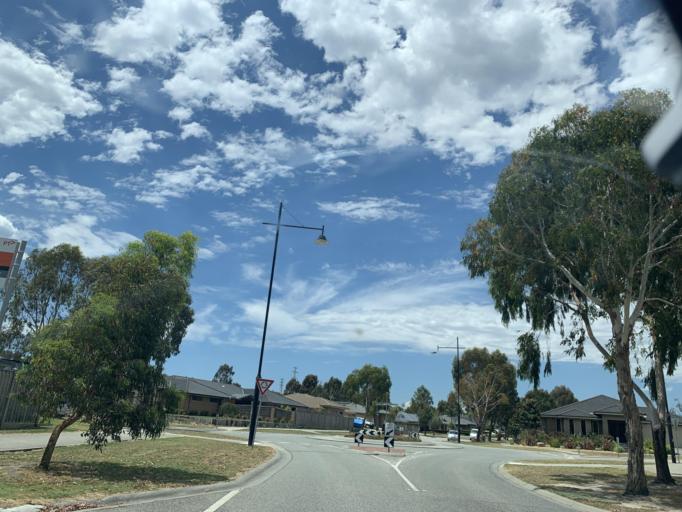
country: AU
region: Victoria
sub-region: Casey
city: Botanic Ridge
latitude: -38.1454
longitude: 145.2551
